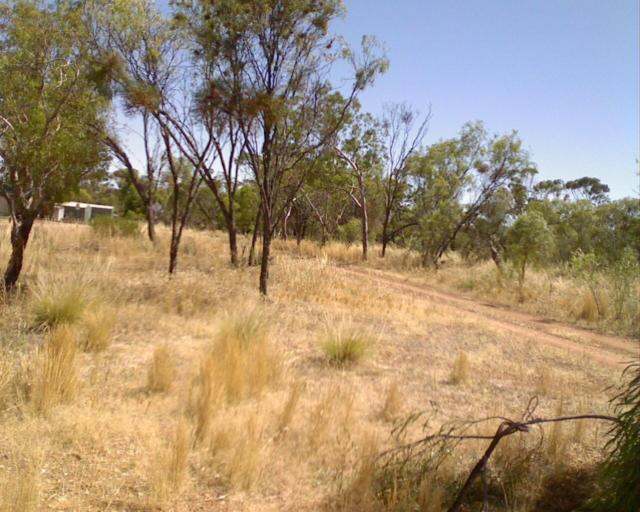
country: AU
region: Western Australia
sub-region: Moora
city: Moora
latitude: -30.3000
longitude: 116.0608
